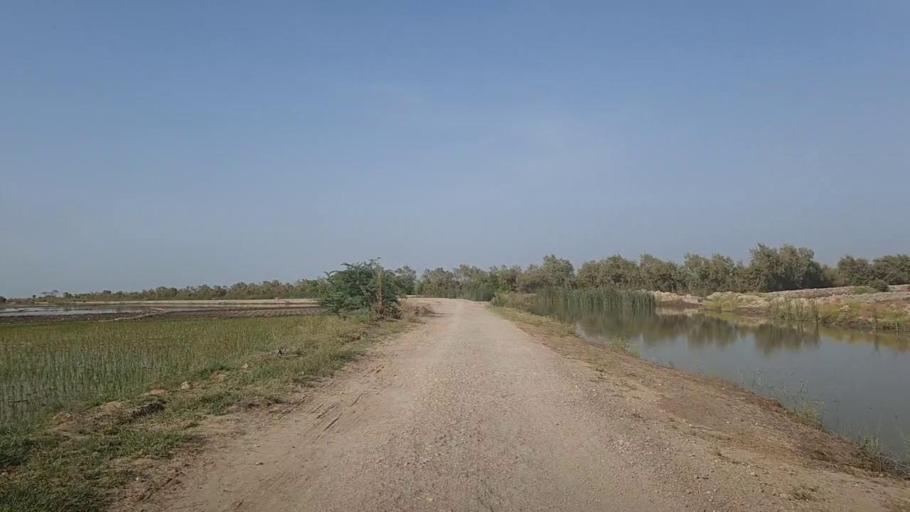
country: PK
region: Sindh
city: Sita Road
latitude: 27.0962
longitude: 67.8723
